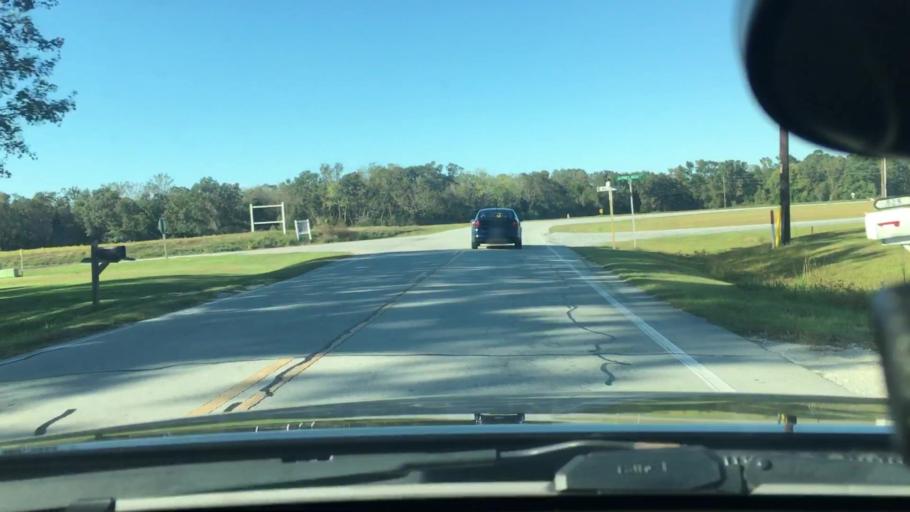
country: US
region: North Carolina
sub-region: Craven County
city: Vanceboro
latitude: 35.2874
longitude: -77.1547
